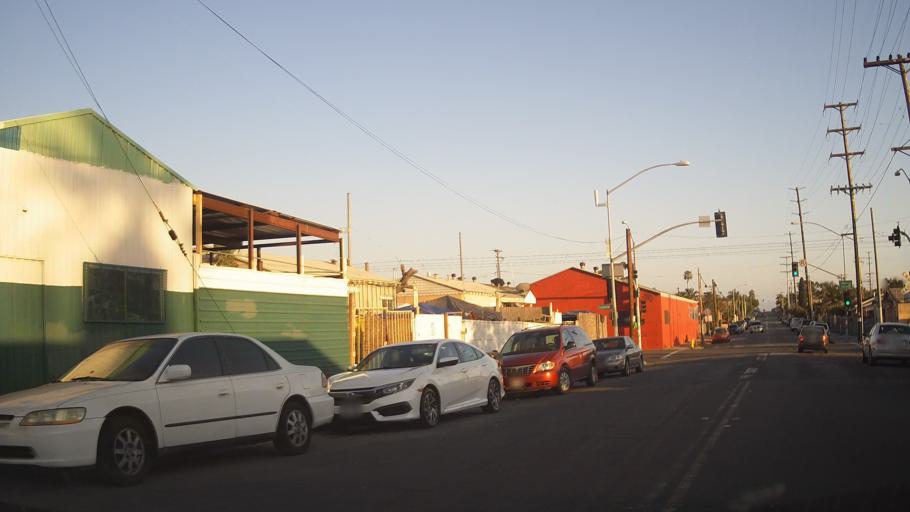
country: US
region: California
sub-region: San Diego County
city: San Diego
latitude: 32.7059
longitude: -117.1339
